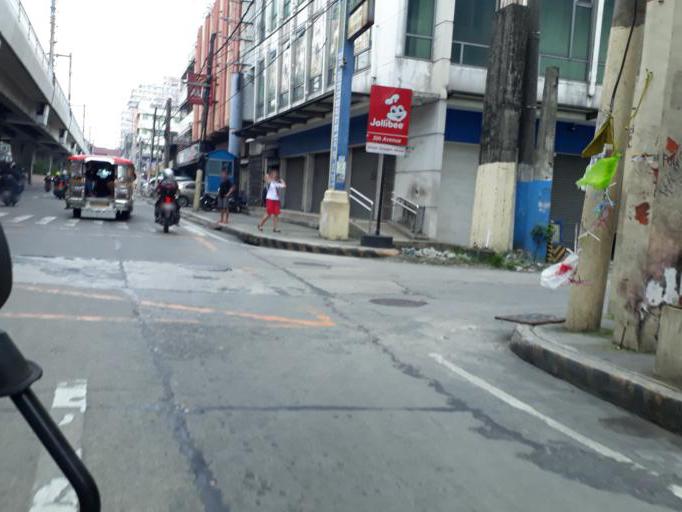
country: PH
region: Calabarzon
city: Del Monte
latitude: 14.6416
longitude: 120.9836
